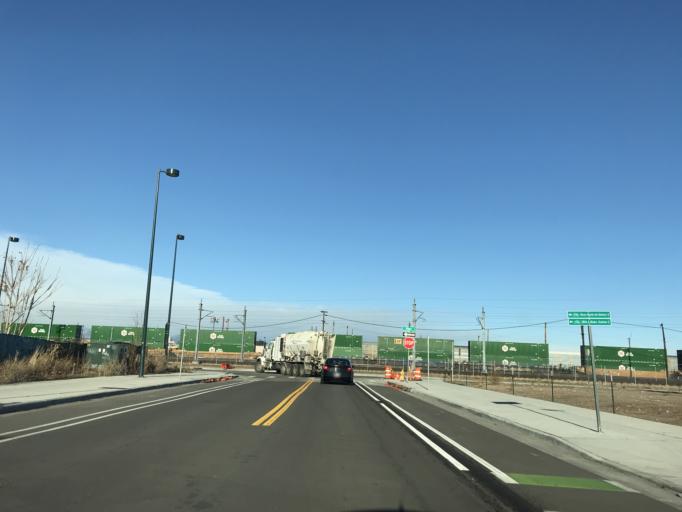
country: US
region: Colorado
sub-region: Denver County
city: Denver
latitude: 39.7721
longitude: -104.9701
